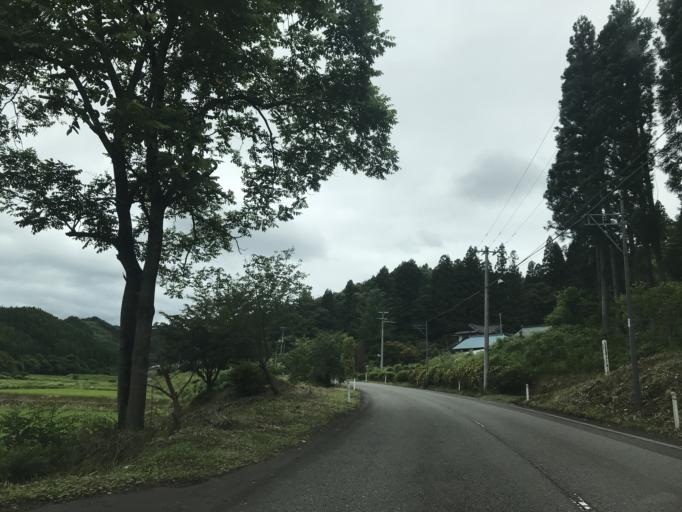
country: JP
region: Iwate
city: Ichinoseki
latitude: 38.9020
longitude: 140.9901
